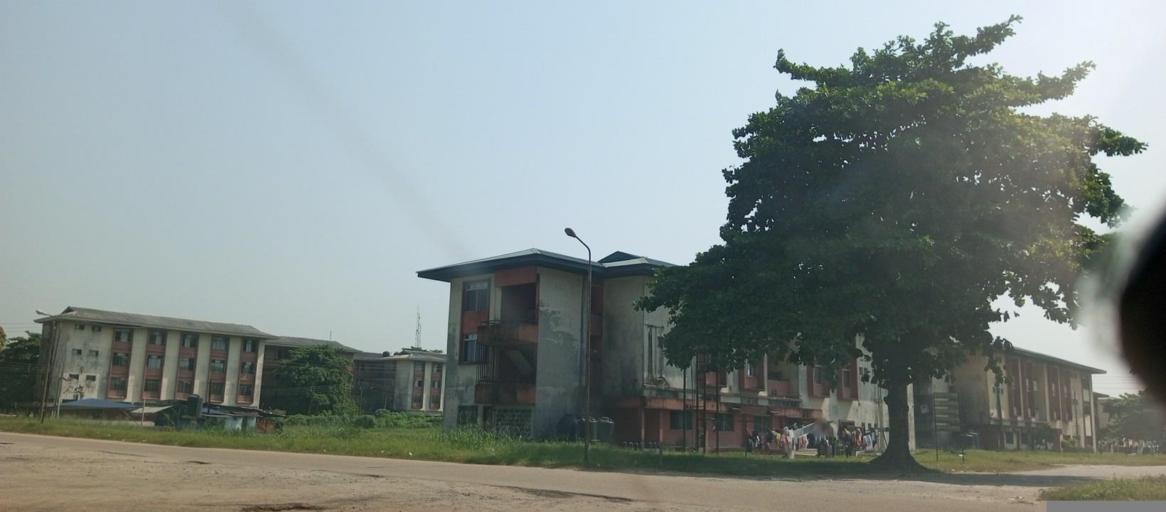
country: NG
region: Rivers
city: Emuoha
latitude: 4.8999
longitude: 6.9216
